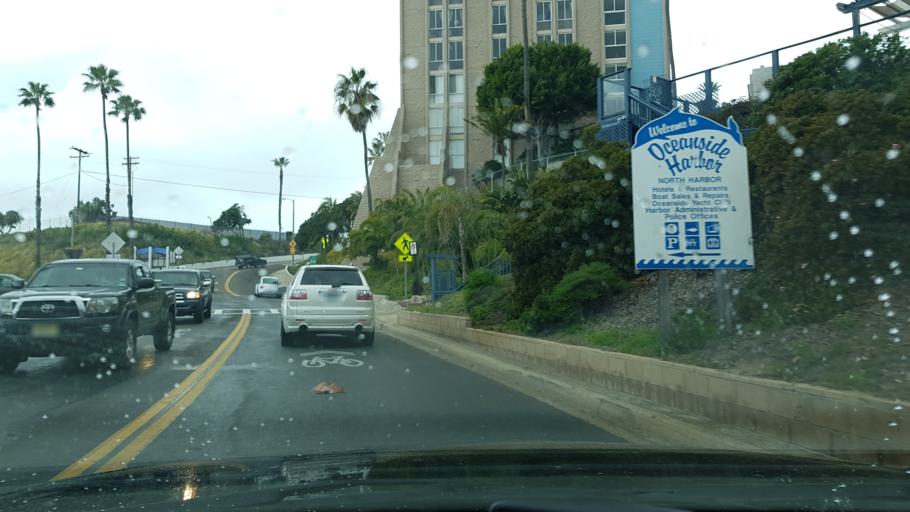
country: US
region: California
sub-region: San Diego County
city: Oceanside
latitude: 33.2066
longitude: -117.3893
